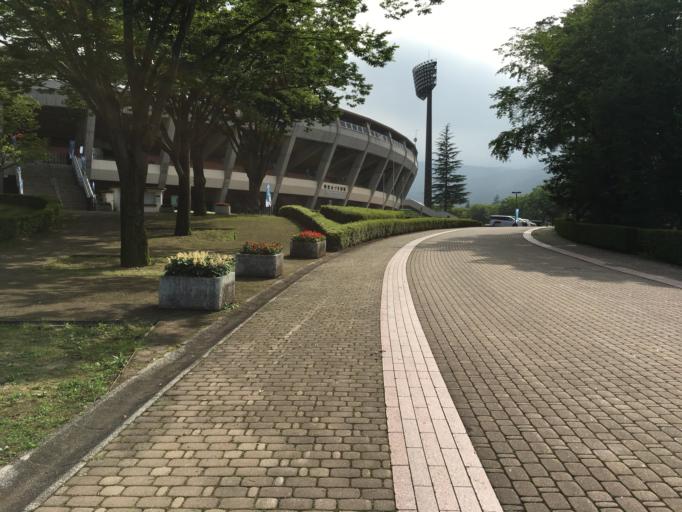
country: JP
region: Fukushima
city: Fukushima-shi
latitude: 37.7227
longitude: 140.3646
